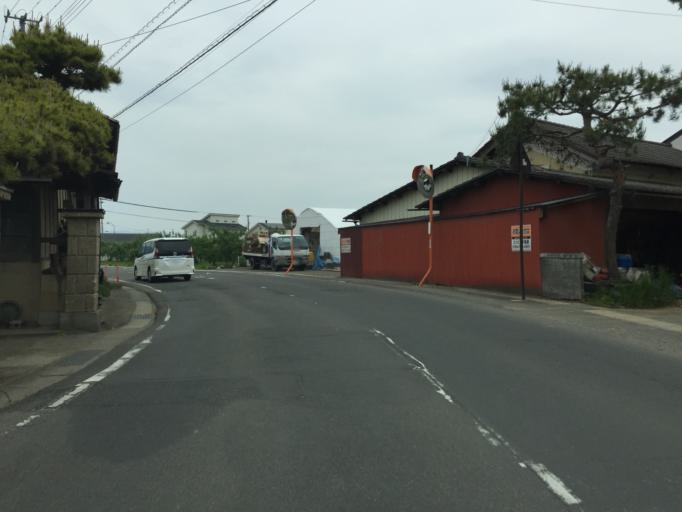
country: JP
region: Fukushima
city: Fukushima-shi
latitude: 37.7963
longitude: 140.4716
